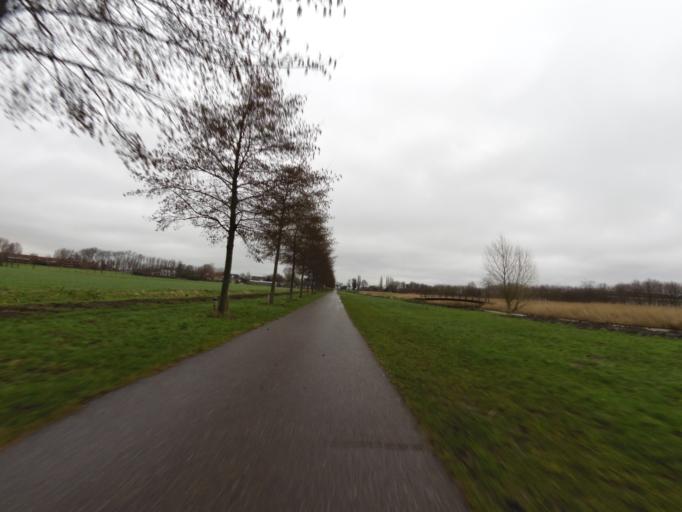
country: NL
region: South Holland
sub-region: Gemeente Maassluis
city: Maassluis
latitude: 51.9174
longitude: 4.2727
